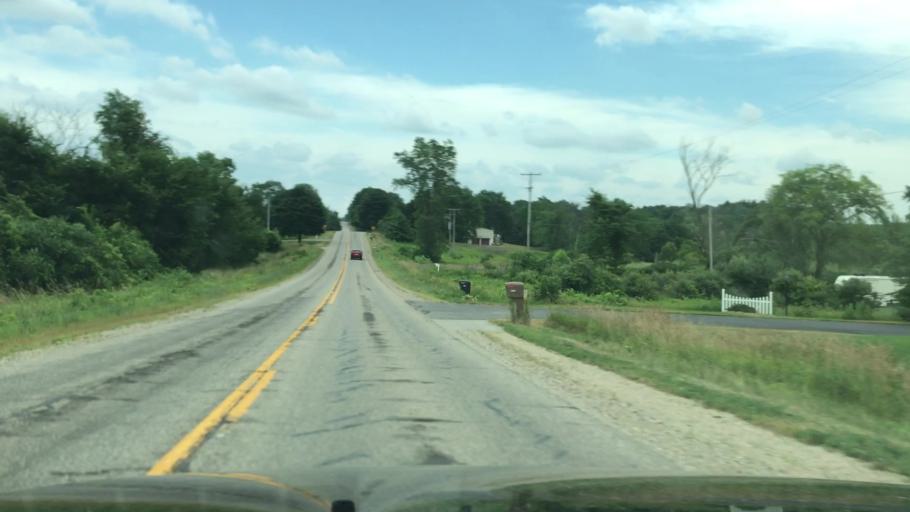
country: US
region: Michigan
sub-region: Ottawa County
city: Hudsonville
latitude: 42.7821
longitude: -85.8478
